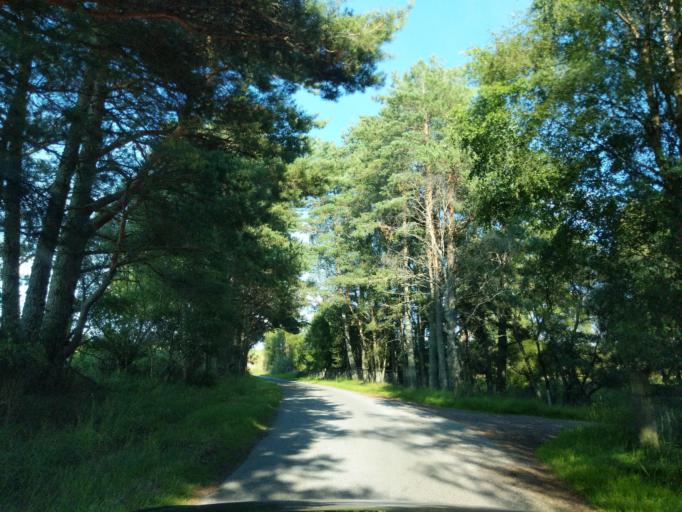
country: GB
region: Scotland
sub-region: Highland
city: Aviemore
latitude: 57.2909
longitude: -3.7483
